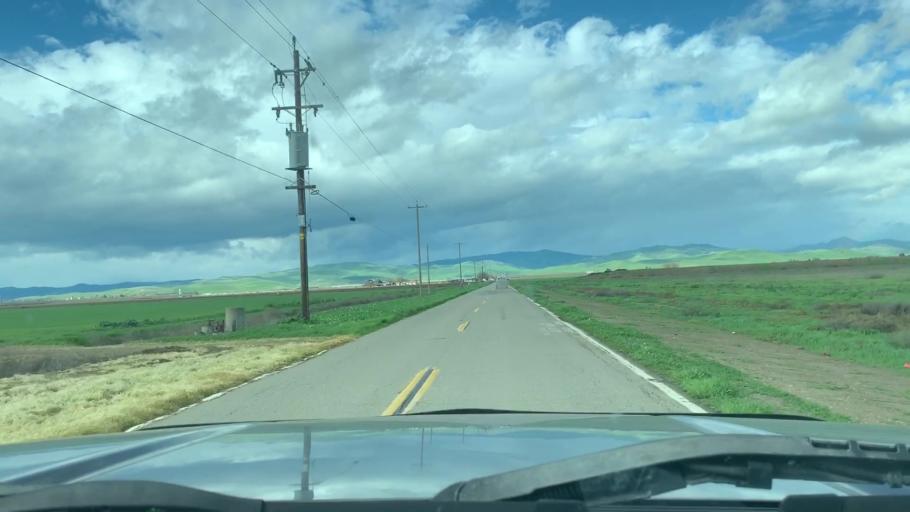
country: US
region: California
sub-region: Merced County
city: Gustine
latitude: 37.1223
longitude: -120.9870
